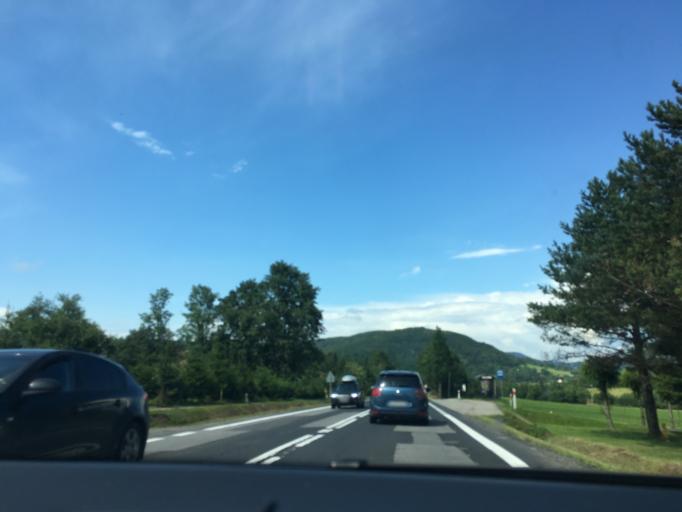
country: PL
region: Subcarpathian Voivodeship
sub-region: Powiat krosnienski
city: Dukla
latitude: 49.4548
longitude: 21.6932
